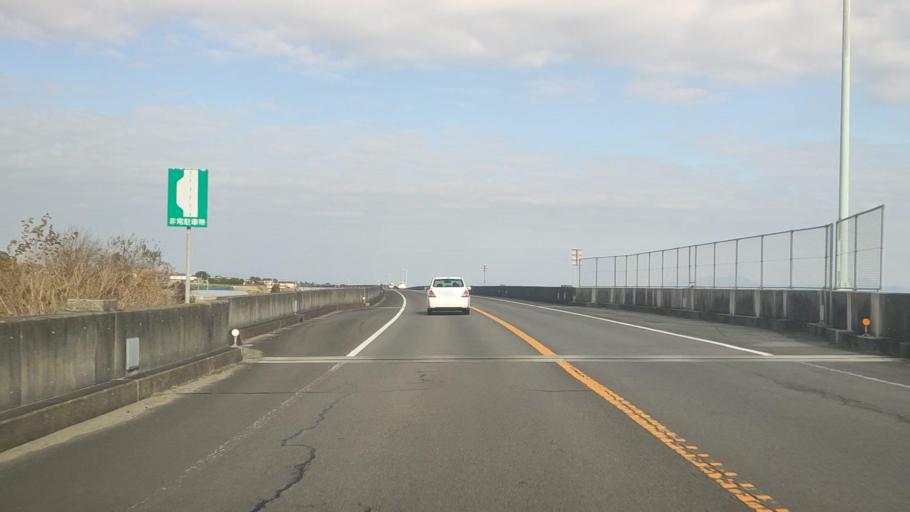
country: JP
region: Nagasaki
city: Shimabara
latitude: 32.7230
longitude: 130.3601
